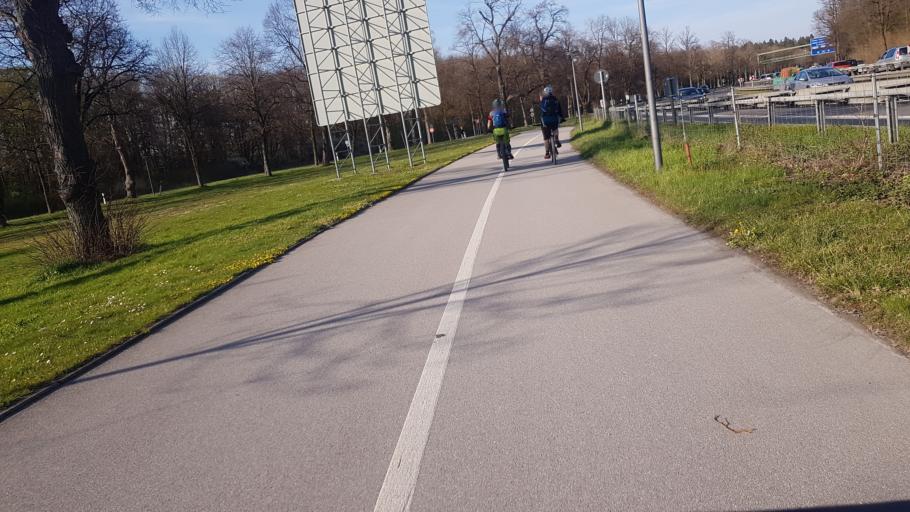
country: DE
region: Bavaria
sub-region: Upper Bavaria
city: Neuried
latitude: 48.0951
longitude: 11.4880
